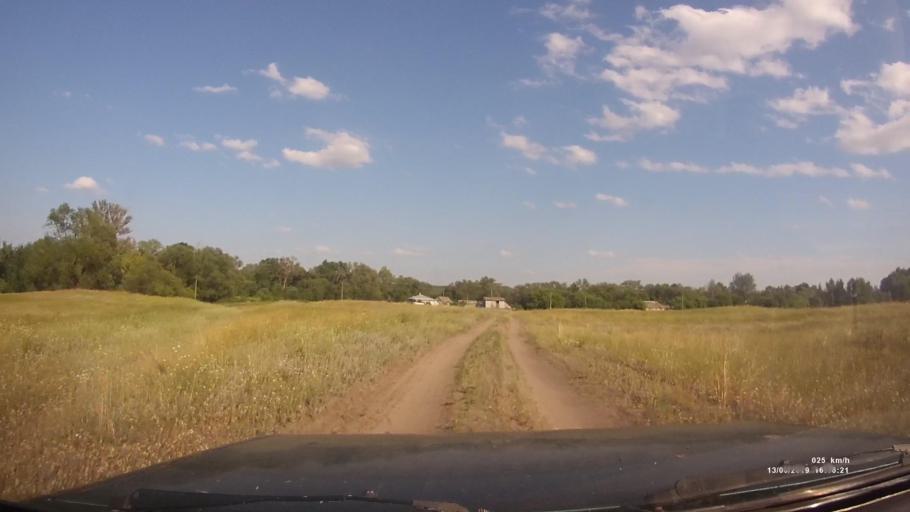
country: RU
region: Rostov
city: Kazanskaya
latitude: 49.9459
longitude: 41.4268
